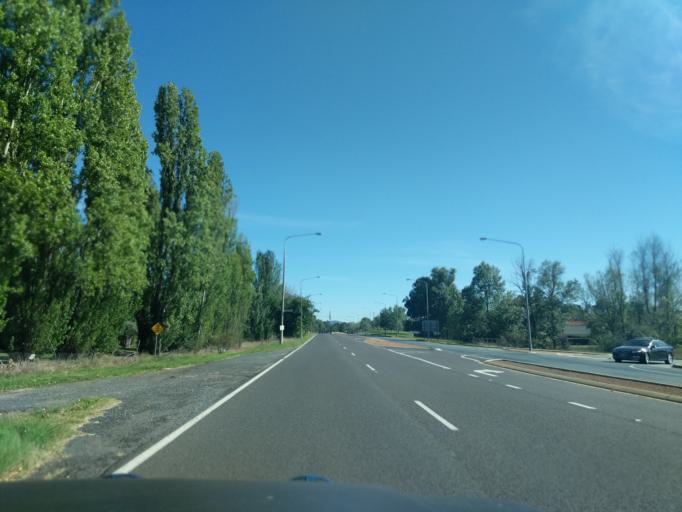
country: AU
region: Australian Capital Territory
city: Forrest
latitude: -35.3419
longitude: 149.1532
